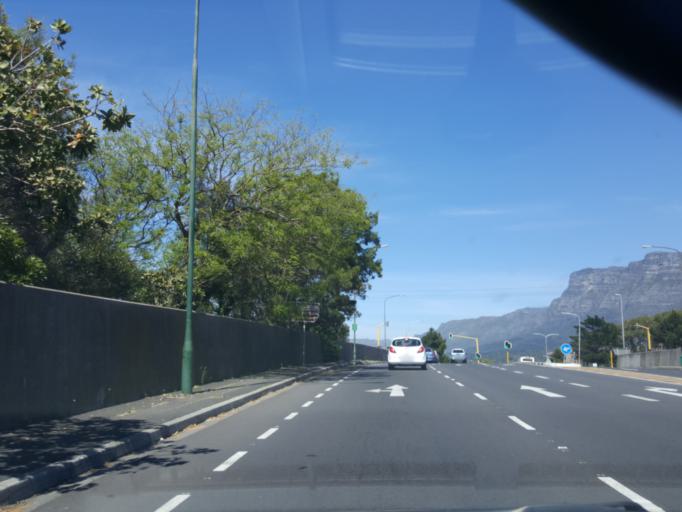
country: ZA
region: Western Cape
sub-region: City of Cape Town
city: Rosebank
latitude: -33.9445
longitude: 18.4923
